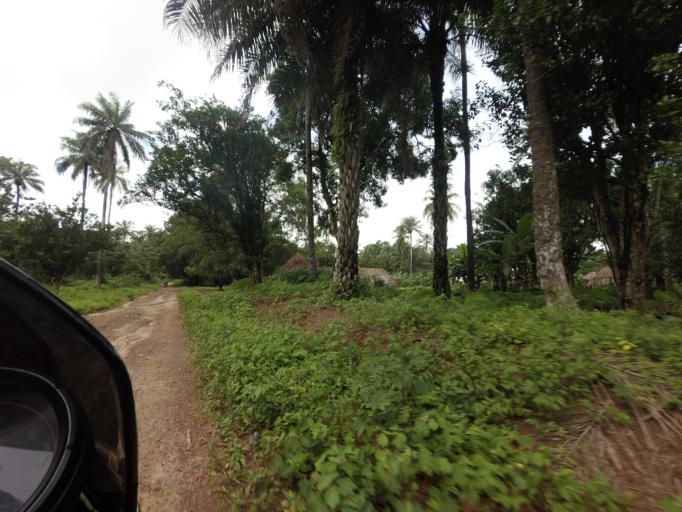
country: SL
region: Northern Province
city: Mambolo
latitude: 8.9897
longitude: -13.0050
